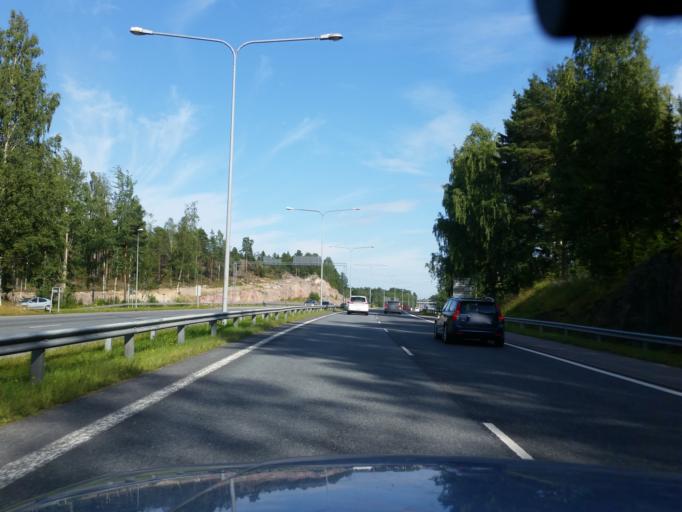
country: FI
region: Uusimaa
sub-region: Helsinki
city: Espoo
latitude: 60.1588
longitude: 24.6243
